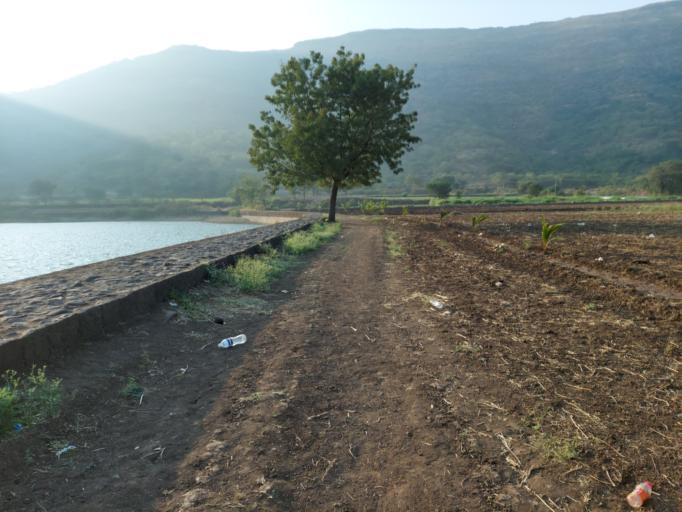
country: IN
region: Maharashtra
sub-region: Pune Division
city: Sasvad
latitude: 18.4192
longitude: 73.9976
